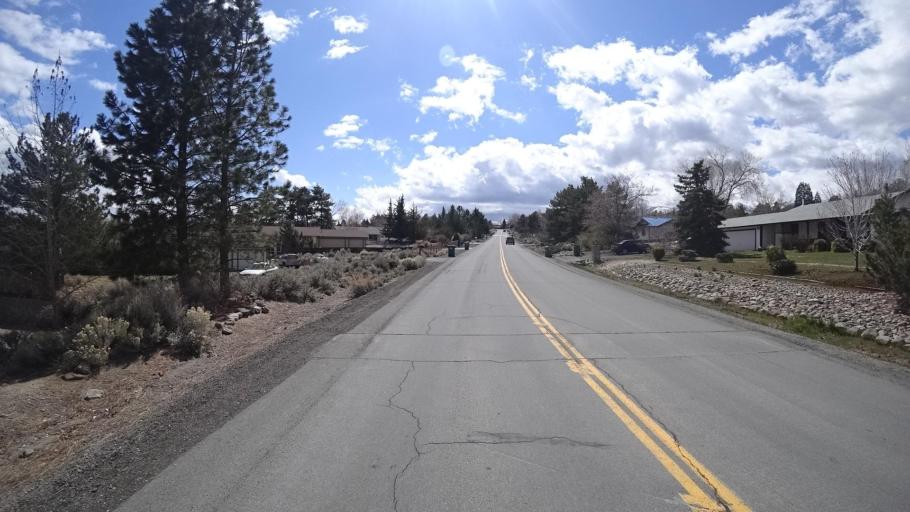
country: US
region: Nevada
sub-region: Washoe County
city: Reno
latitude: 39.4156
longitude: -119.7880
